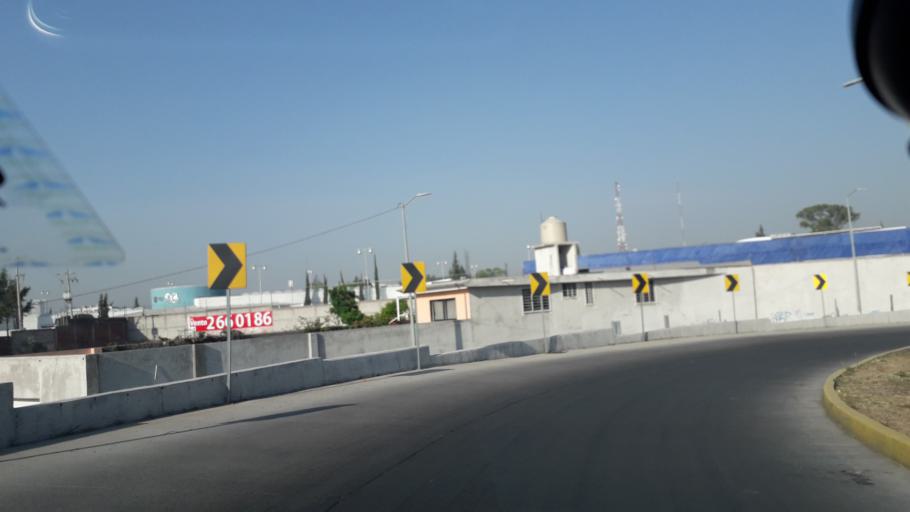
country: MX
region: Puebla
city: Tlazcalancingo
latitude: 19.0348
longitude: -98.2567
